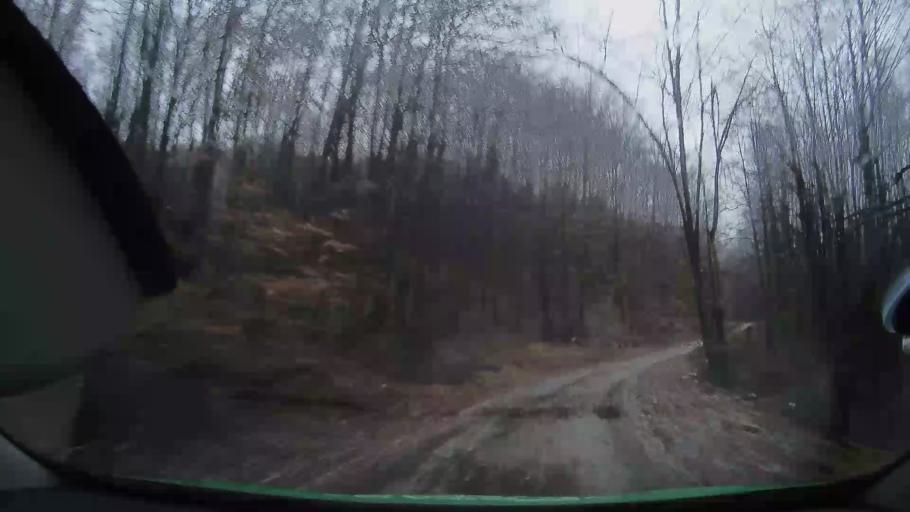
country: RO
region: Alba
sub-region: Comuna Avram Iancu
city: Avram Iancu
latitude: 46.3136
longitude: 22.7923
